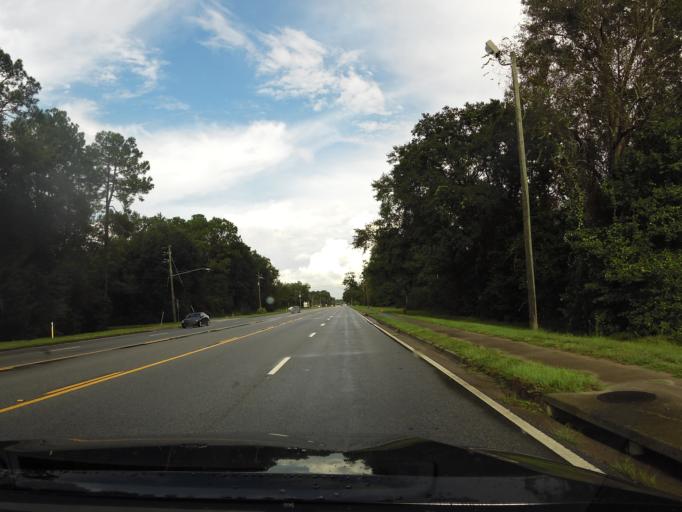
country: US
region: Georgia
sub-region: Liberty County
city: Walthourville
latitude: 31.7792
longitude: -81.6226
